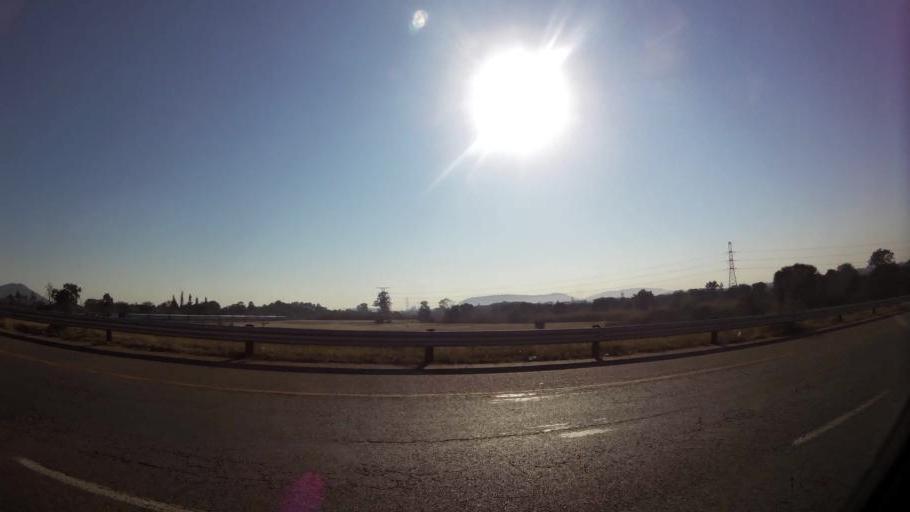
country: ZA
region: Gauteng
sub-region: City of Tshwane Metropolitan Municipality
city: Pretoria
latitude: -25.6581
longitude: 28.1855
